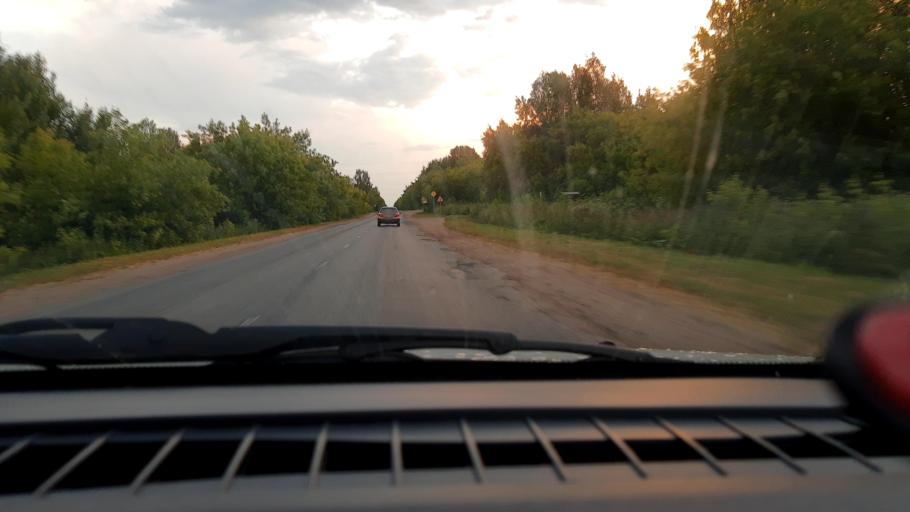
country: RU
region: Nizjnij Novgorod
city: Kstovo
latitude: 56.1343
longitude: 44.0946
